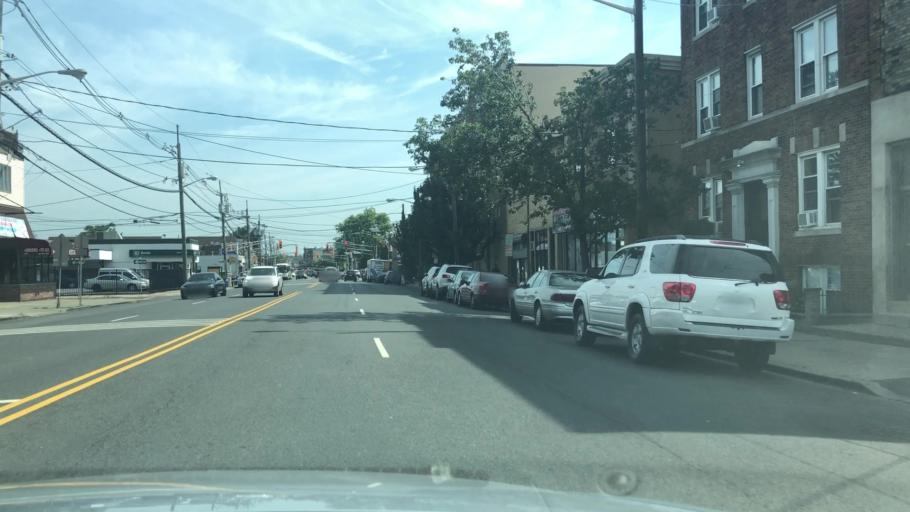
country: US
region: New Jersey
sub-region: Hudson County
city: North Bergen
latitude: 40.8027
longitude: -74.0124
